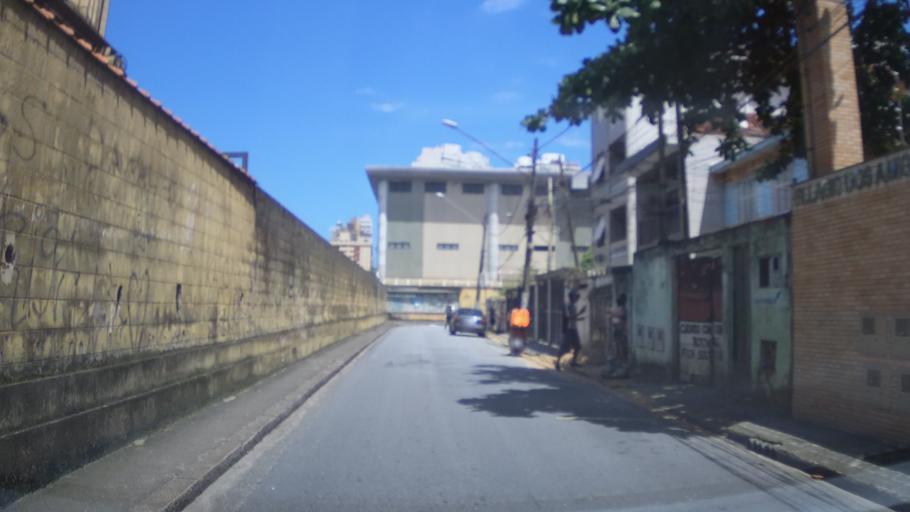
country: BR
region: Sao Paulo
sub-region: Santos
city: Santos
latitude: -23.9590
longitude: -46.3355
